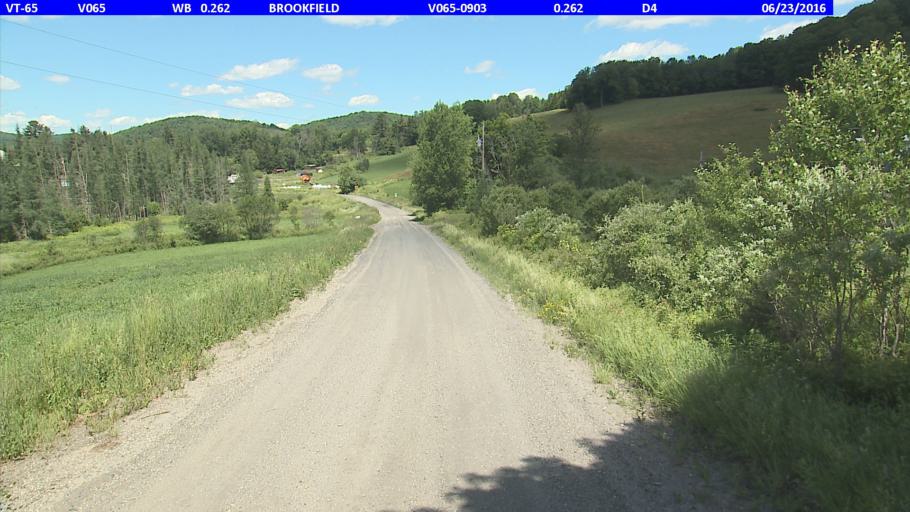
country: US
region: Vermont
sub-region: Washington County
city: Northfield
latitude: 44.0649
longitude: -72.6301
